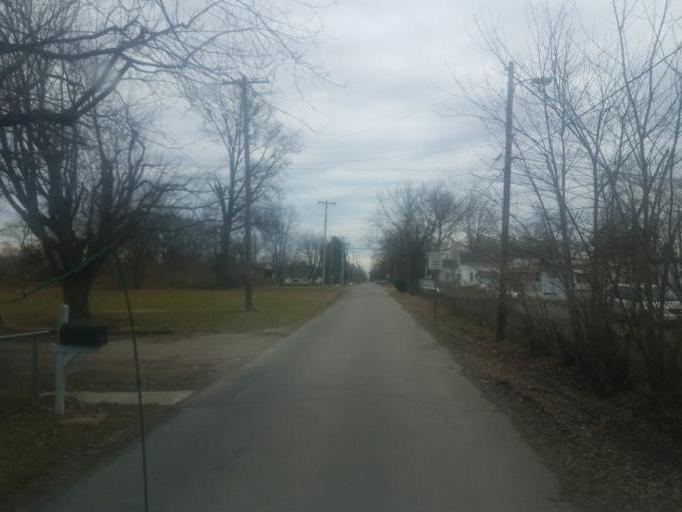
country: US
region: Ohio
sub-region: Marion County
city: Marion
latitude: 40.6084
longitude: -83.1286
